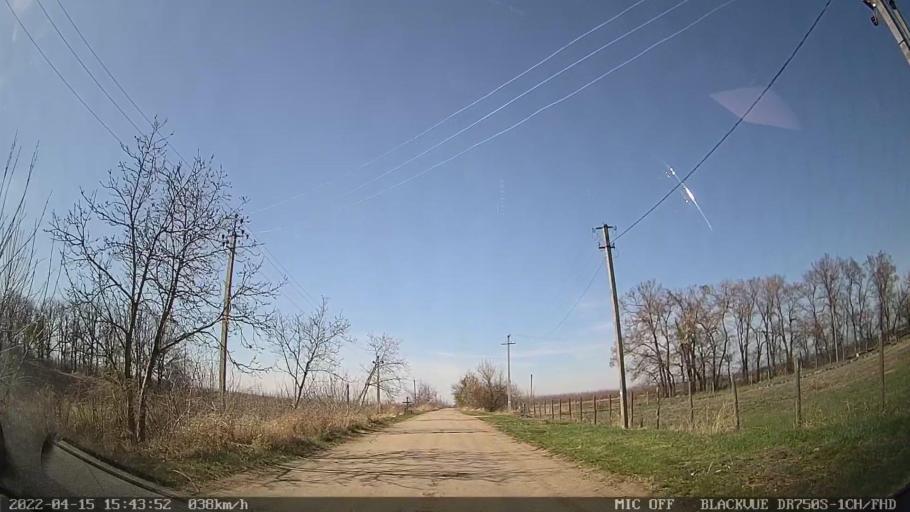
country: MD
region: Raionul Ocnita
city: Otaci
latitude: 48.3672
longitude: 27.9247
